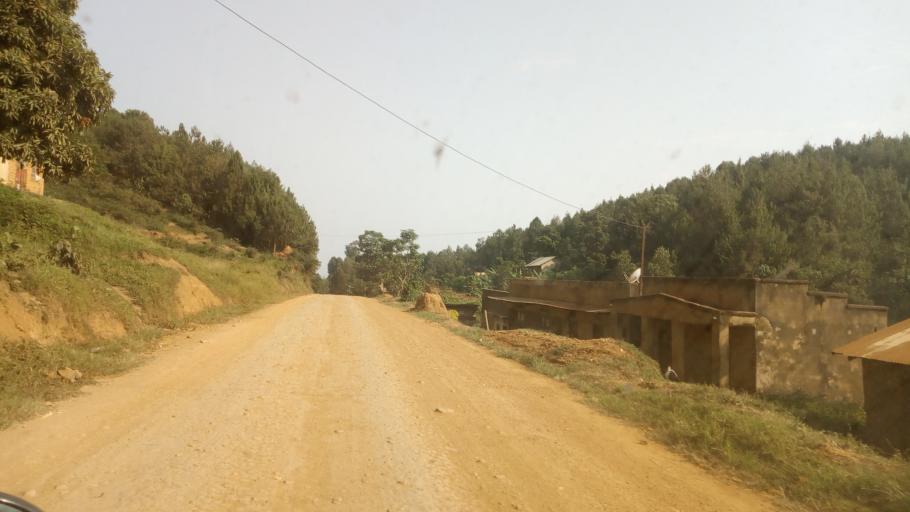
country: UG
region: Western Region
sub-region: Kanungu District
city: Ntungamo
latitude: -0.8288
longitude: 29.7085
